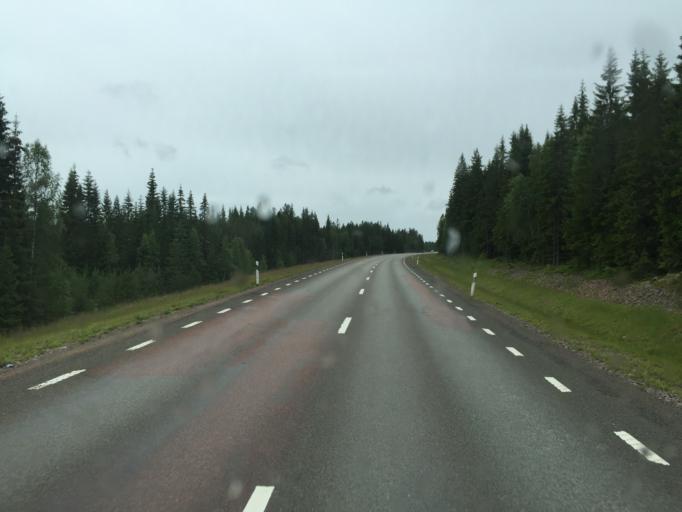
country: SE
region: Dalarna
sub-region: Malung-Saelens kommun
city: Malung
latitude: 60.5877
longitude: 13.5804
